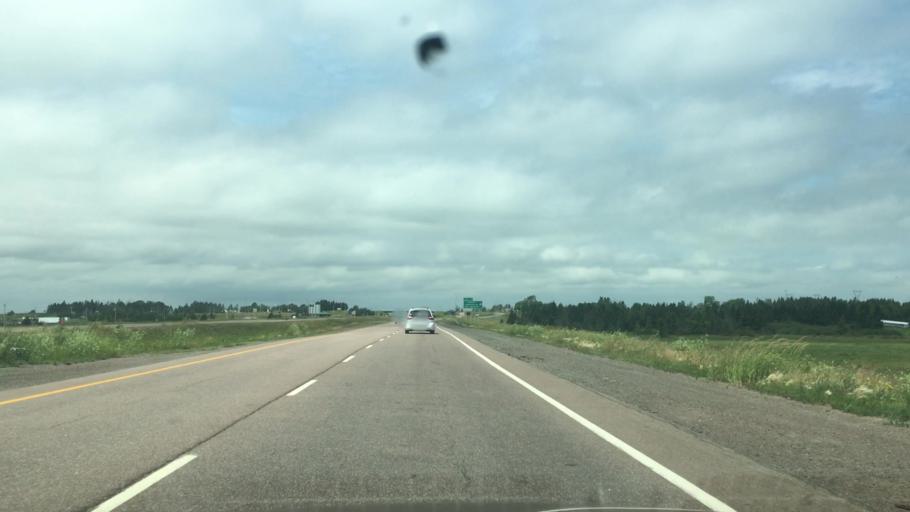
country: CA
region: Nova Scotia
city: Amherst
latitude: 45.8478
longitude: -64.2434
